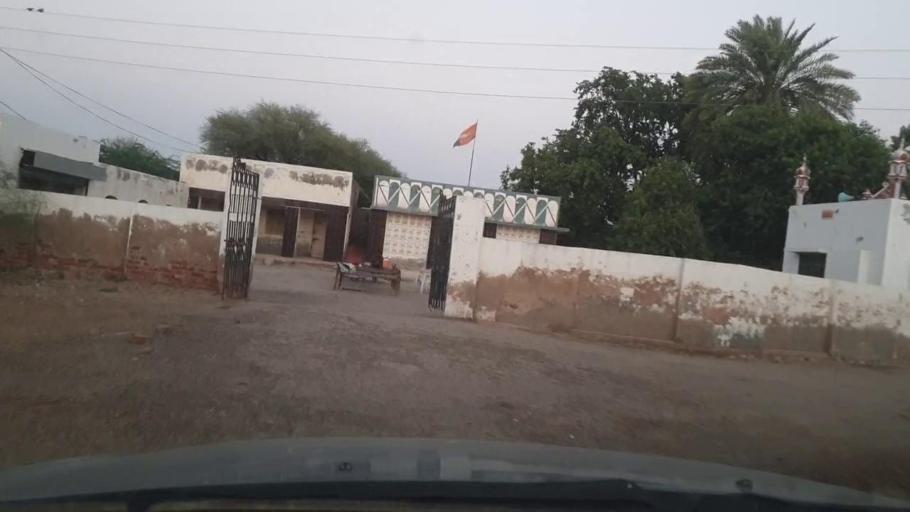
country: PK
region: Sindh
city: Digri
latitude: 25.1207
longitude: 69.0066
